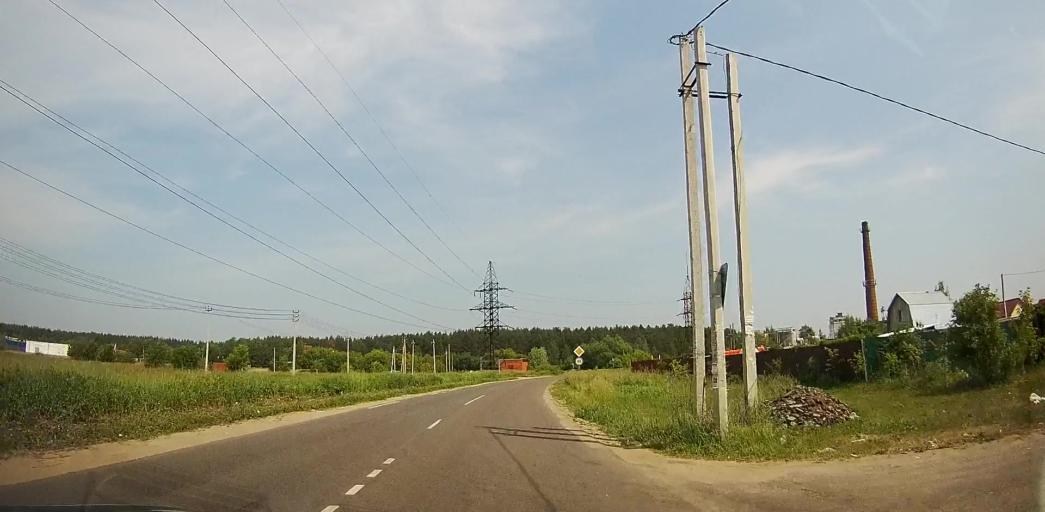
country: RU
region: Moskovskaya
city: Malyshevo
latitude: 55.5038
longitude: 38.3224
